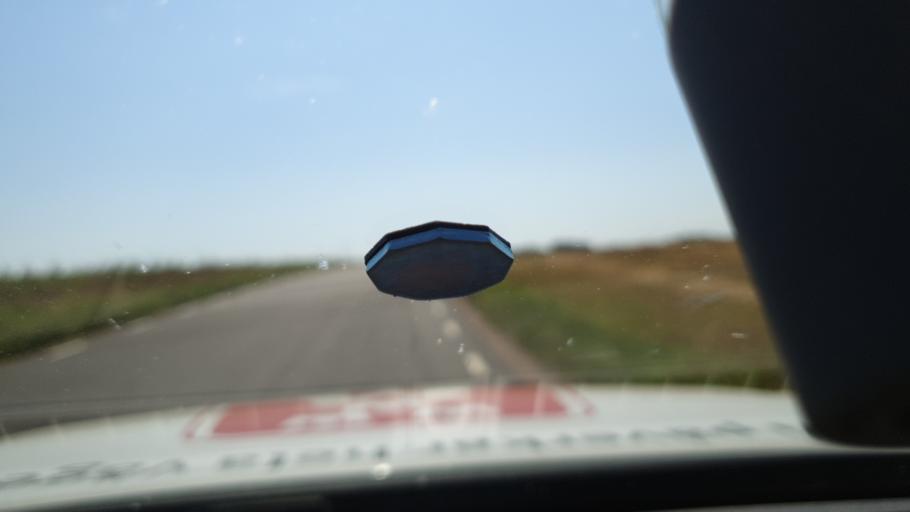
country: SE
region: Skane
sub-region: Sjobo Kommun
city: Blentarp
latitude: 55.5558
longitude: 13.5614
